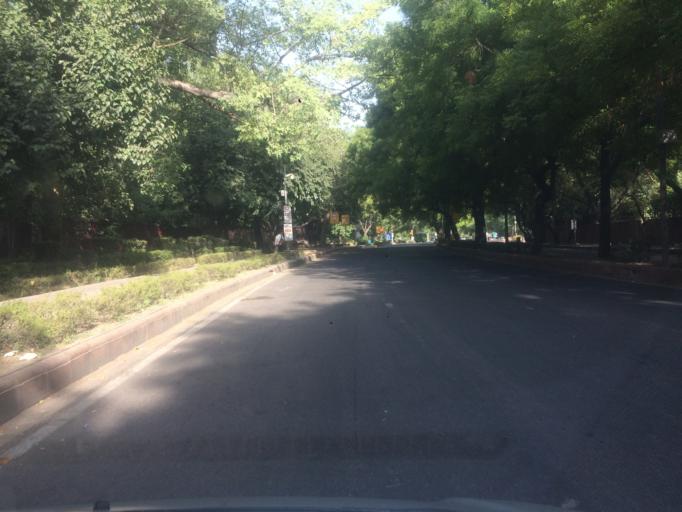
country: IN
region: NCT
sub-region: New Delhi
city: New Delhi
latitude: 28.6093
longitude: 77.2388
